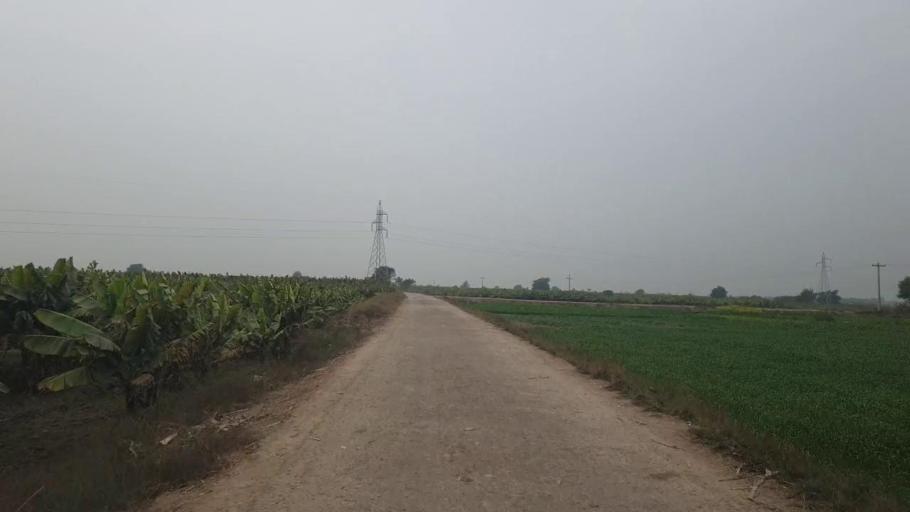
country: PK
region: Sindh
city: Shahdadpur
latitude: 25.8640
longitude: 68.6232
